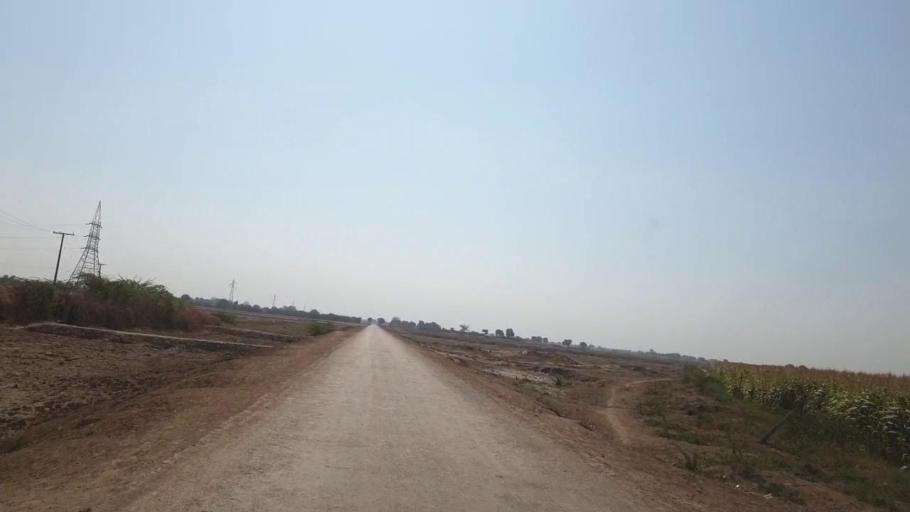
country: PK
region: Sindh
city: Kunri
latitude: 25.1717
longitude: 69.5436
